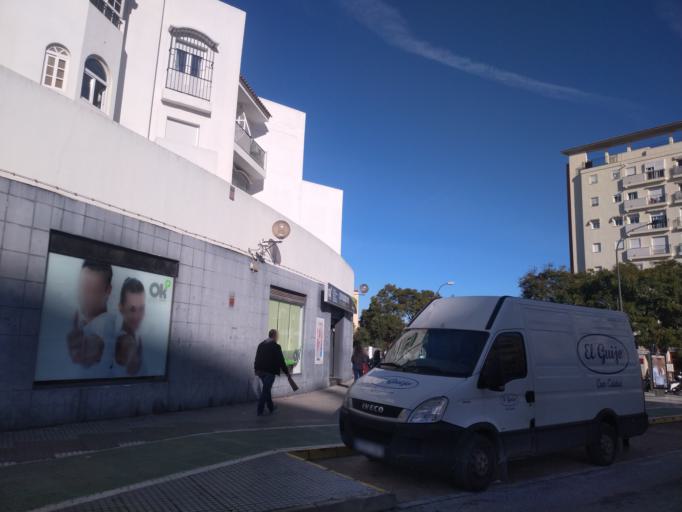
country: ES
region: Andalusia
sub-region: Provincia de Cadiz
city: San Fernando
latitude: 36.4695
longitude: -6.1996
